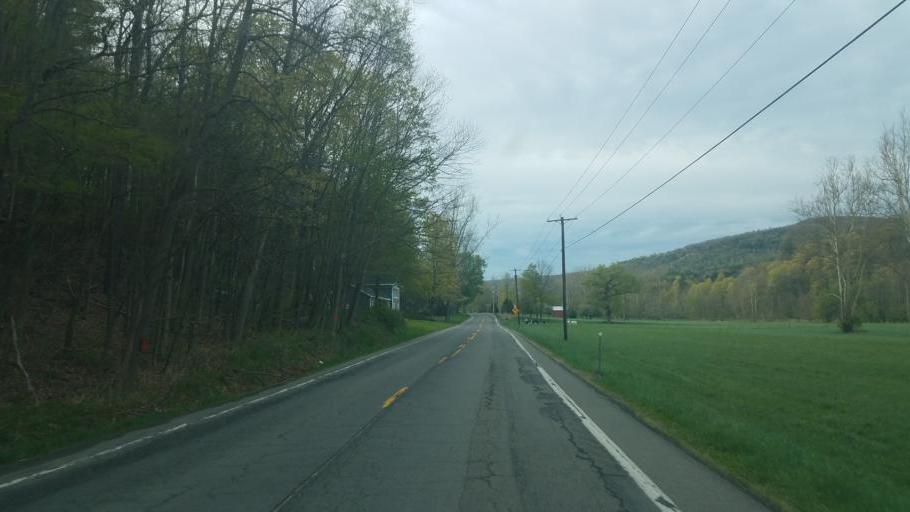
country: US
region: New York
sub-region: Steuben County
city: Canisteo
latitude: 42.2340
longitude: -77.5777
